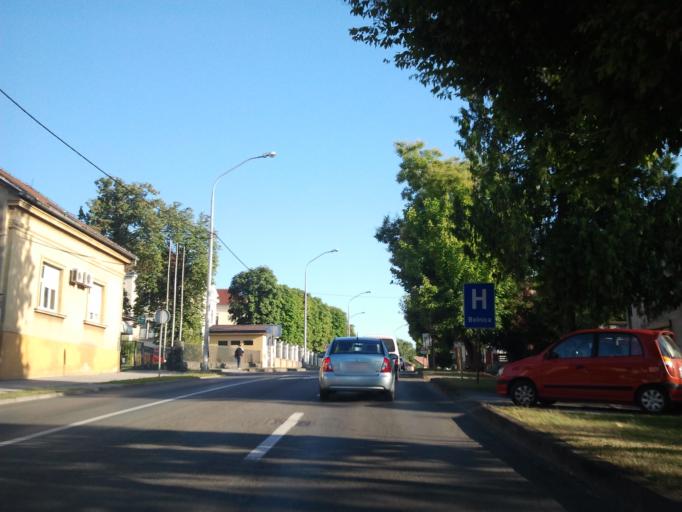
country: HR
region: Sisacko-Moslavacka
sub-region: Grad Sisak
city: Sisak
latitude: 45.4776
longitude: 16.3678
